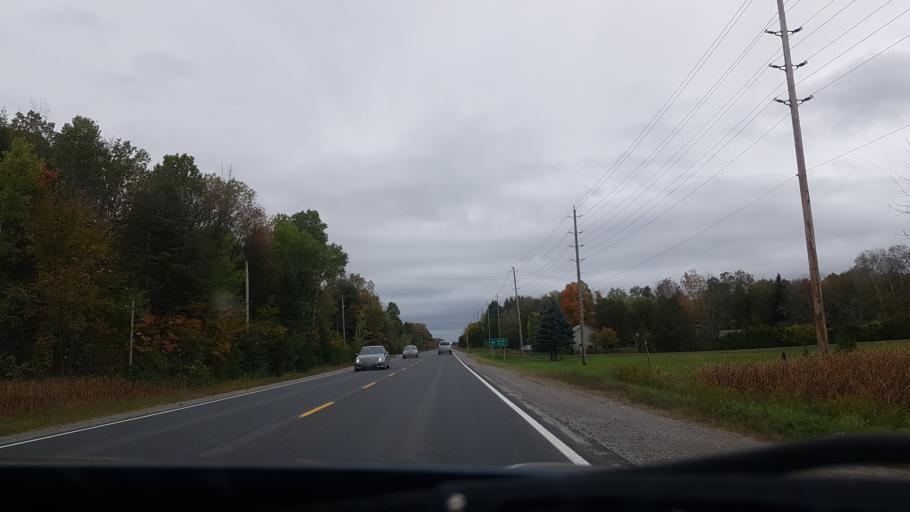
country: CA
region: Ontario
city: Omemee
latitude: 44.1969
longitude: -78.4802
